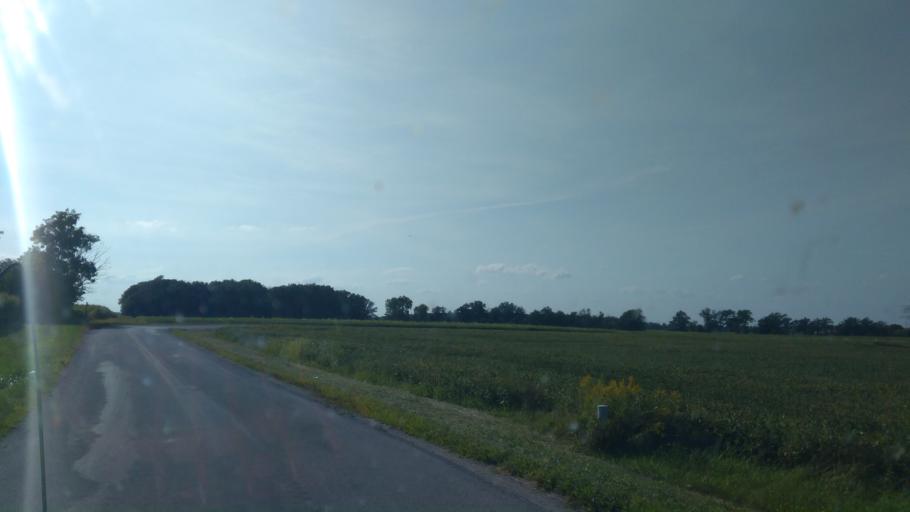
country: US
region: Ohio
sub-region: Hardin County
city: Forest
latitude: 40.7345
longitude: -83.5751
